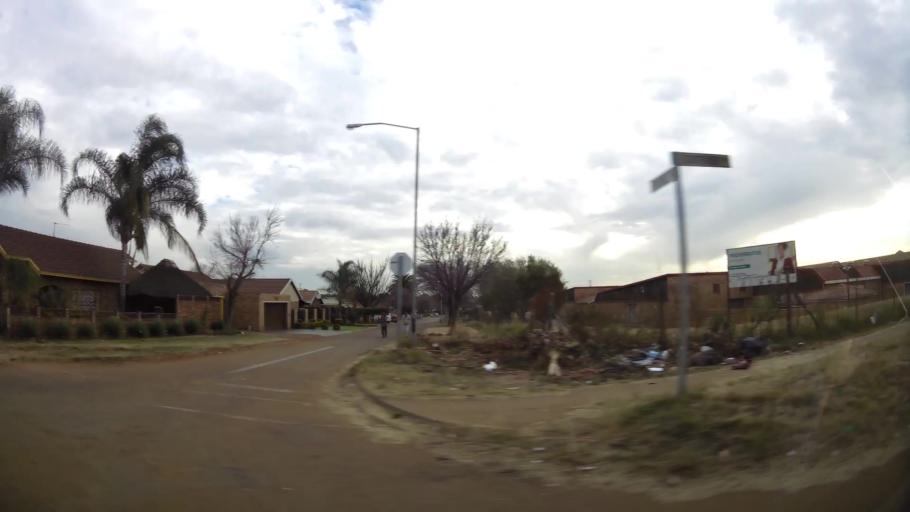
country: ZA
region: Gauteng
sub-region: City of Tshwane Metropolitan Municipality
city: Pretoria
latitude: -25.7029
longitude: 28.3047
